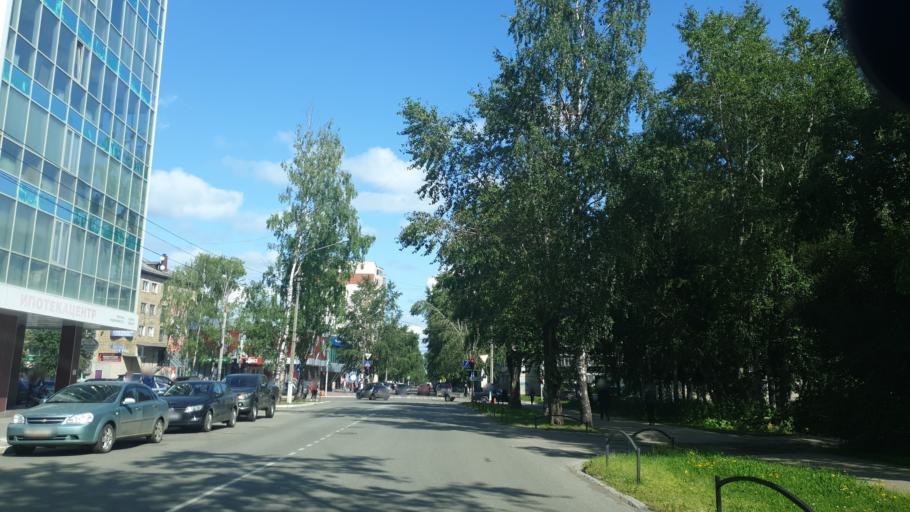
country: RU
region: Komi Republic
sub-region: Syktyvdinskiy Rayon
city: Syktyvkar
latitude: 61.6639
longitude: 50.8313
